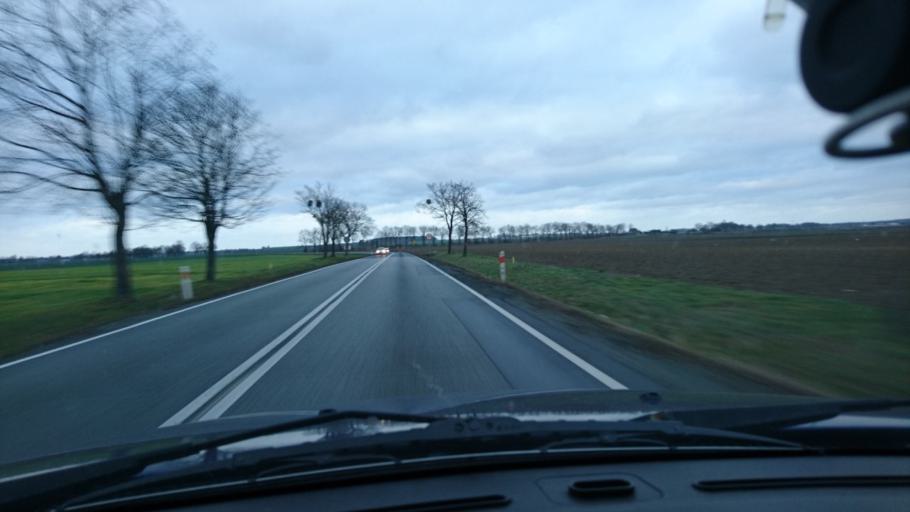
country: PL
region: Opole Voivodeship
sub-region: Powiat kluczborski
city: Byczyna
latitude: 51.0670
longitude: 18.2028
